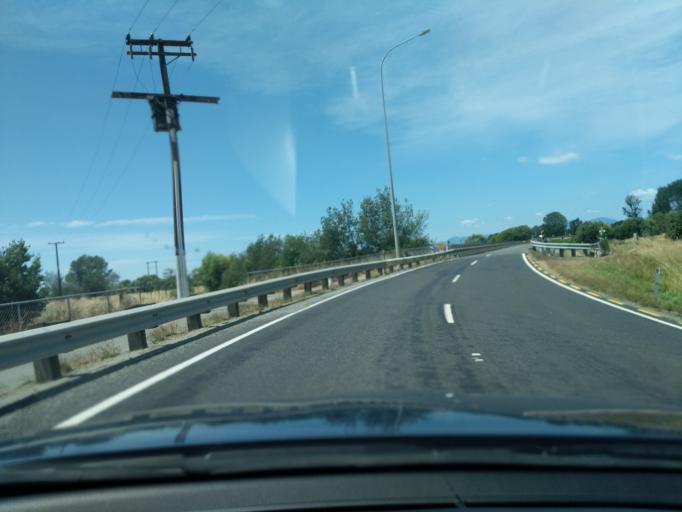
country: NZ
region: Tasman
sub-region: Tasman District
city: Motueka
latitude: -41.0902
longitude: 173.0079
